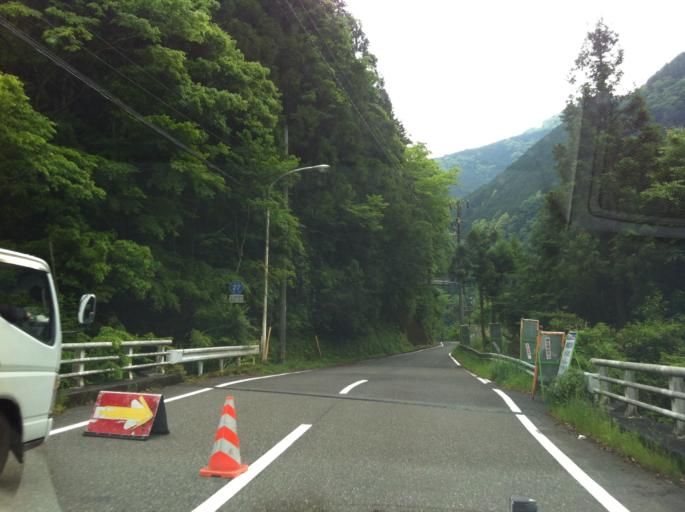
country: JP
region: Shizuoka
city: Shizuoka-shi
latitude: 35.1736
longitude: 138.3128
